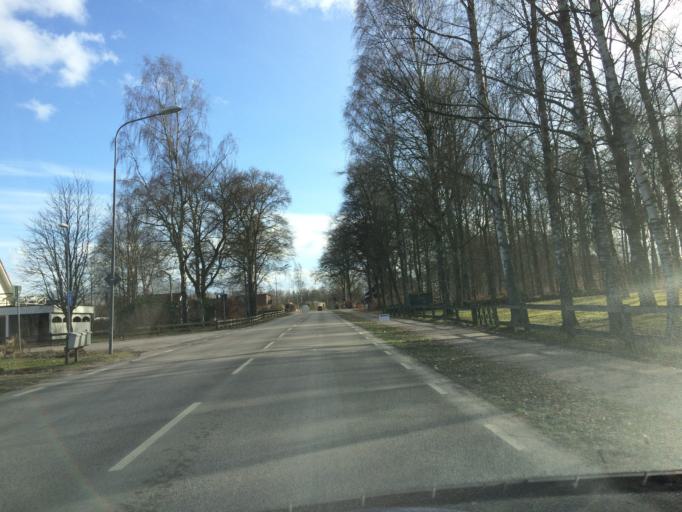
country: SE
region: Kronoberg
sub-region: Almhults Kommun
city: AElmhult
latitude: 56.5615
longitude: 14.1307
